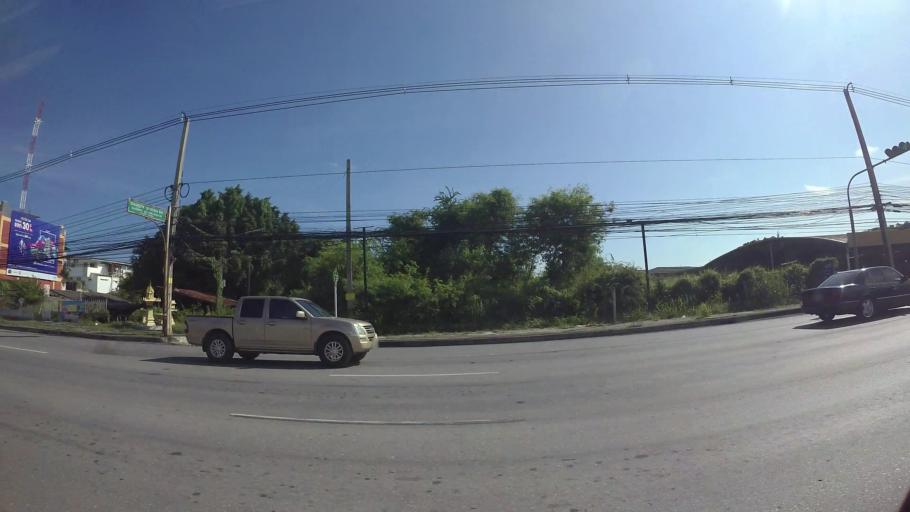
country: TH
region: Rayong
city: Rayong
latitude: 12.6702
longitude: 101.2940
